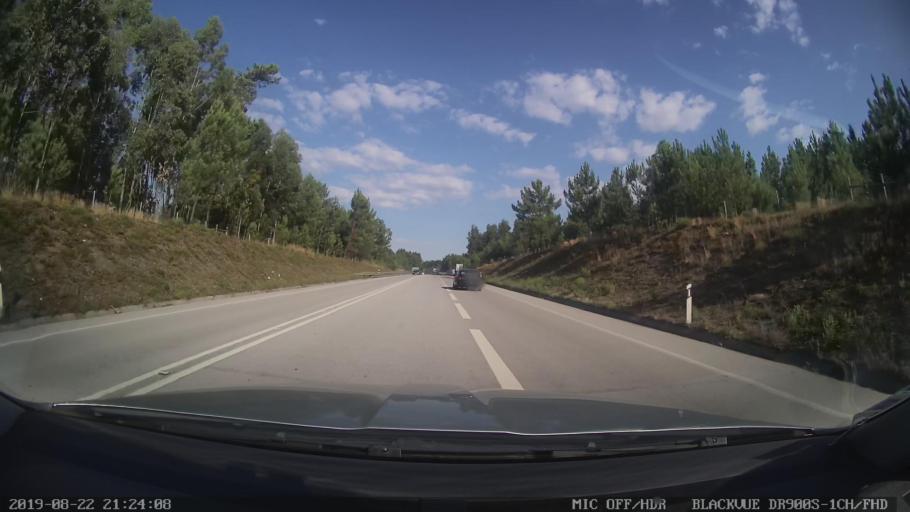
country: PT
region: Castelo Branco
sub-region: Serta
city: Serta
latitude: 39.8384
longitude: -8.1179
